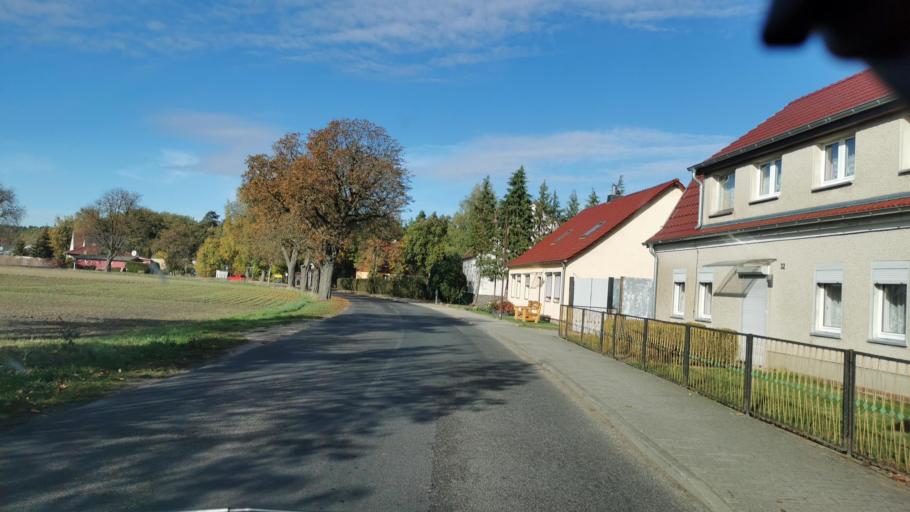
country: DE
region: Brandenburg
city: Melchow
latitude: 52.7571
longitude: 13.7846
